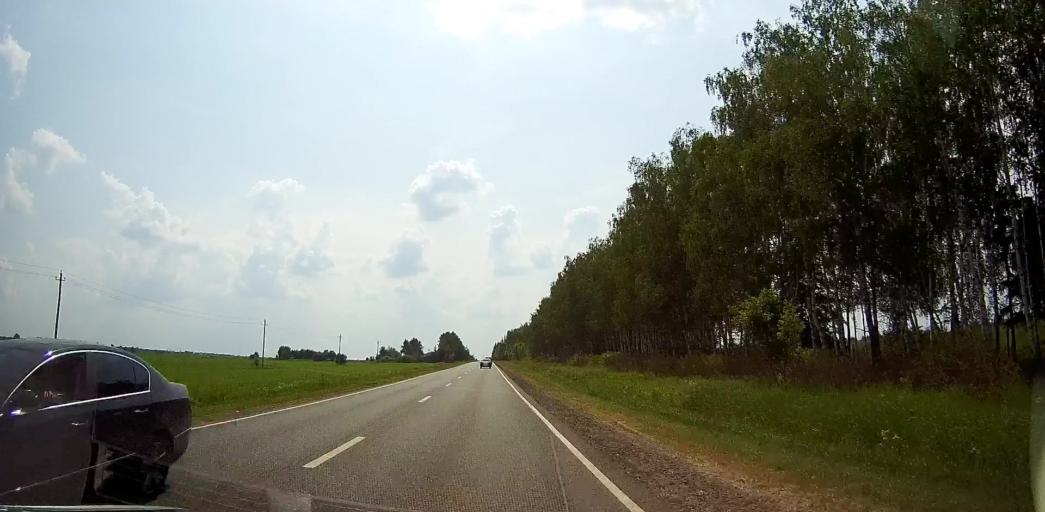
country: RU
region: Moskovskaya
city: Malino
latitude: 55.0819
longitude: 38.1667
